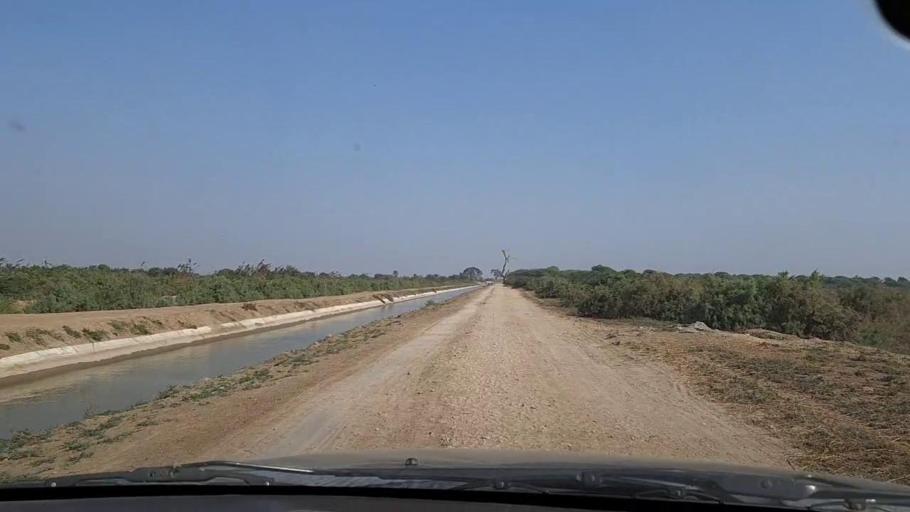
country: PK
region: Sindh
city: Mirpur Sakro
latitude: 24.3420
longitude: 67.7269
